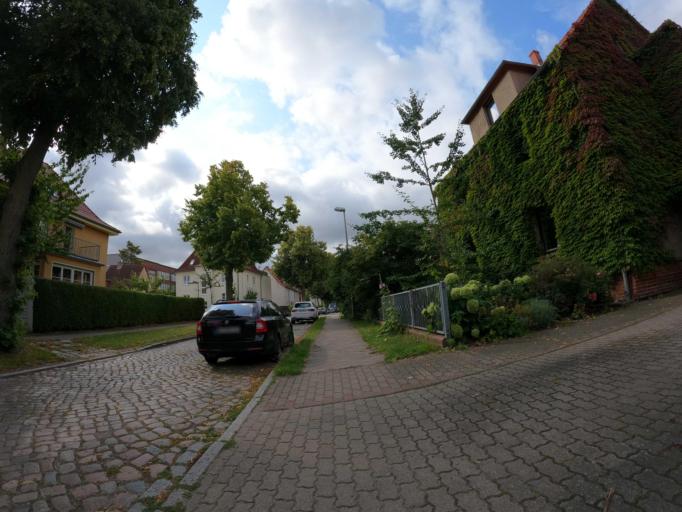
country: DE
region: Mecklenburg-Vorpommern
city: Stralsund
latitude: 54.3202
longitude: 13.0770
